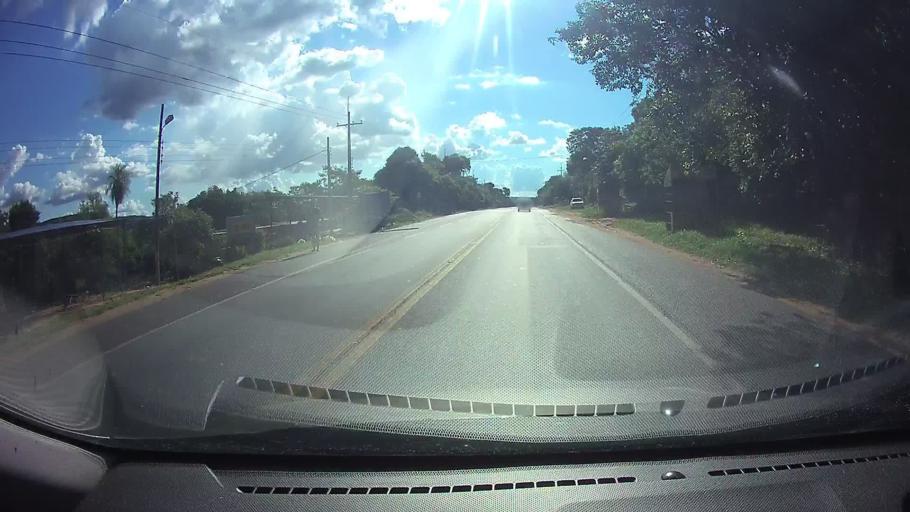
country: PY
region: Cordillera
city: Caacupe
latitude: -25.3882
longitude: -57.1068
